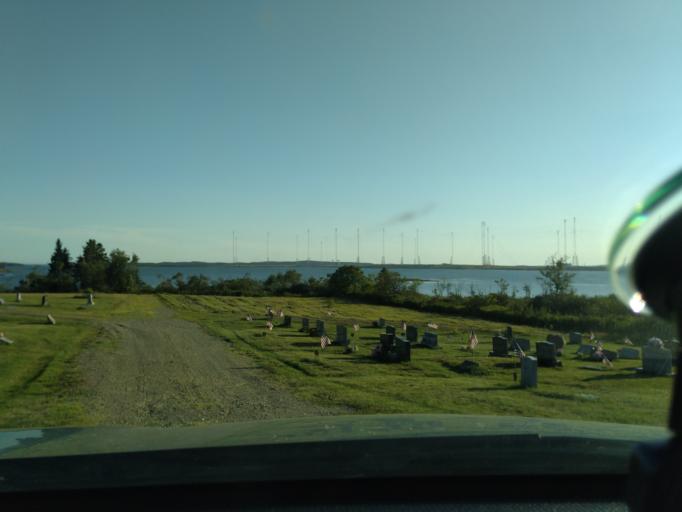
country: US
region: Maine
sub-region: Washington County
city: Machiasport
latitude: 44.6692
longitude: -67.2429
